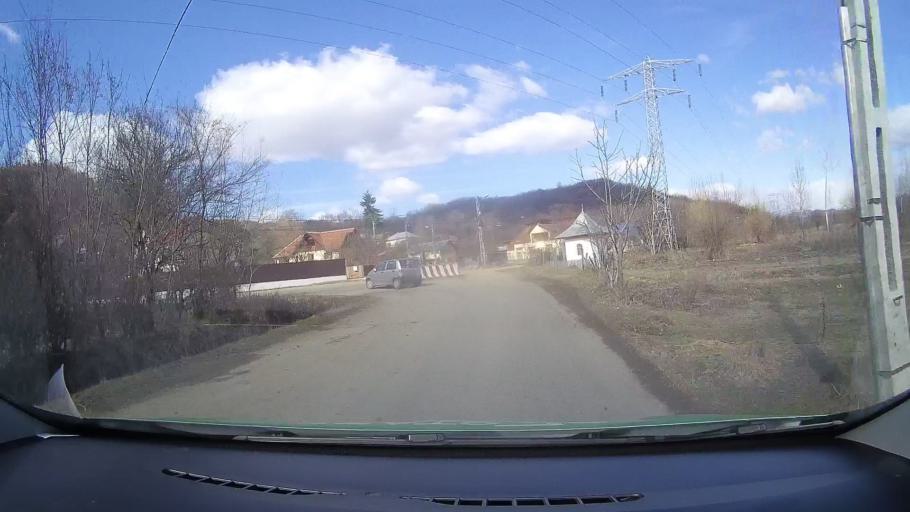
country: RO
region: Dambovita
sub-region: Oras Pucioasa
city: Pucioasa
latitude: 45.0679
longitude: 25.4238
